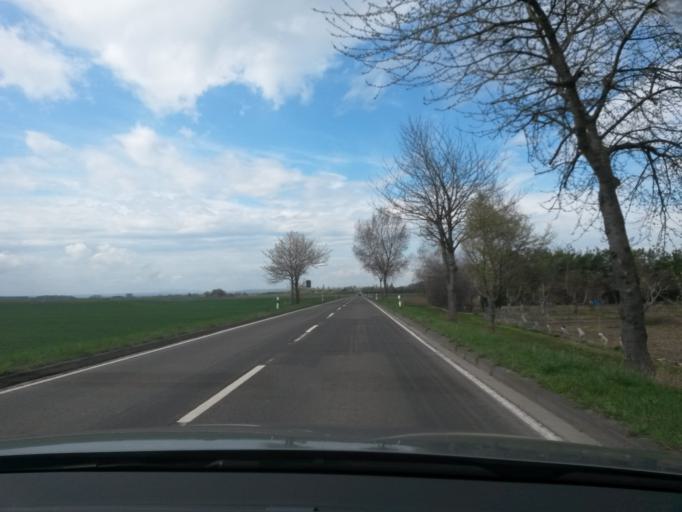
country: DE
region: Hesse
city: Biebesheim
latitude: 49.7505
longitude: 8.4473
